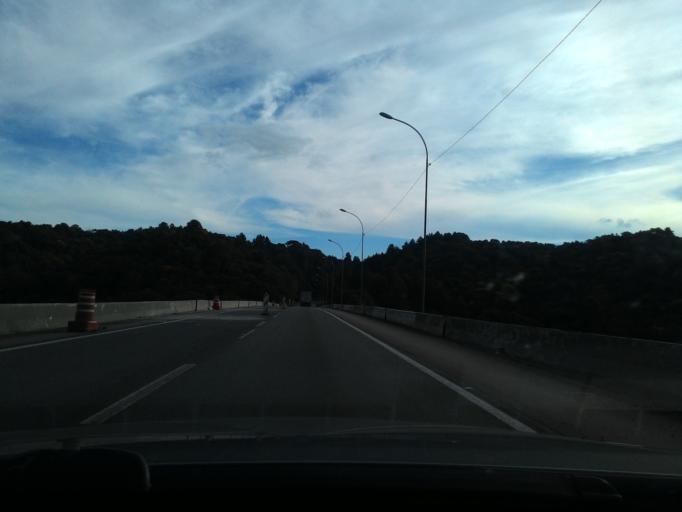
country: BR
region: Parana
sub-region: Campina Grande Do Sul
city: Campina Grande do Sul
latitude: -25.1789
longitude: -48.8801
